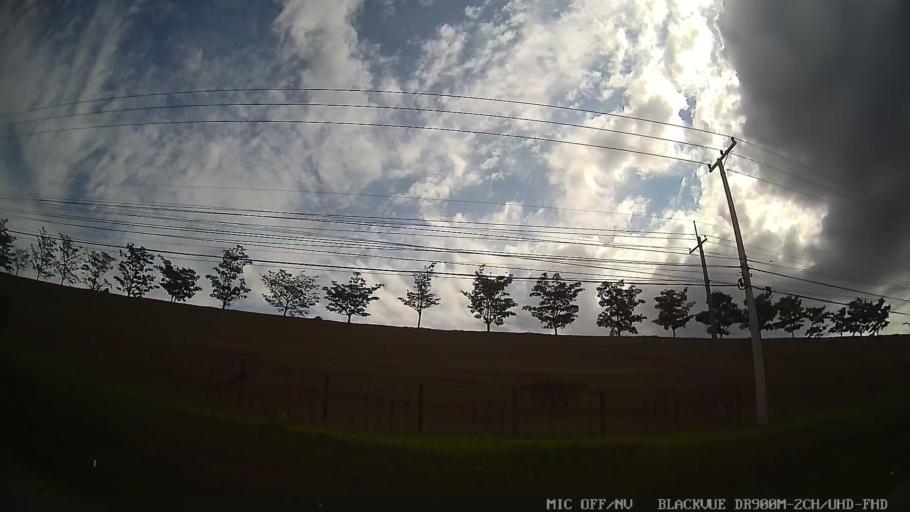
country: BR
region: Sao Paulo
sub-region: Indaiatuba
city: Indaiatuba
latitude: -23.1389
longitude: -47.2447
